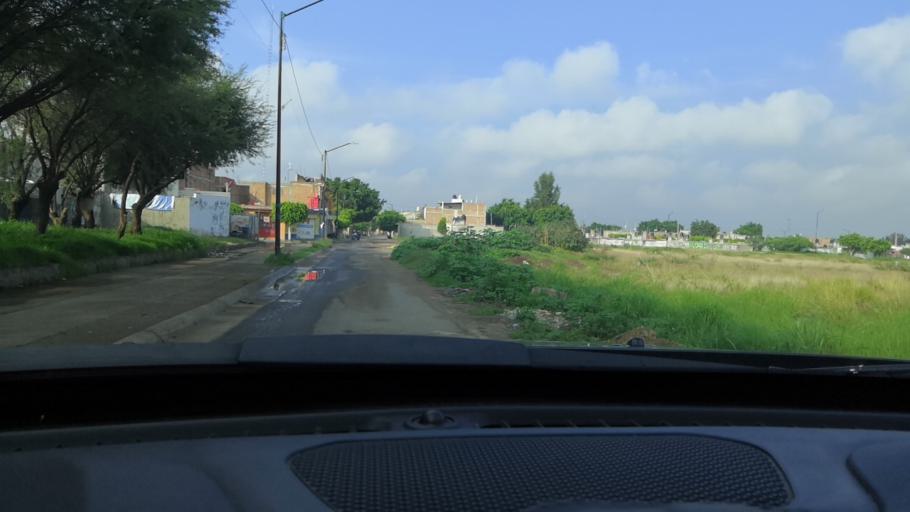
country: MX
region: Guanajuato
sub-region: Leon
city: Fraccionamiento Paraiso Real
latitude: 21.1023
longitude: -101.5878
